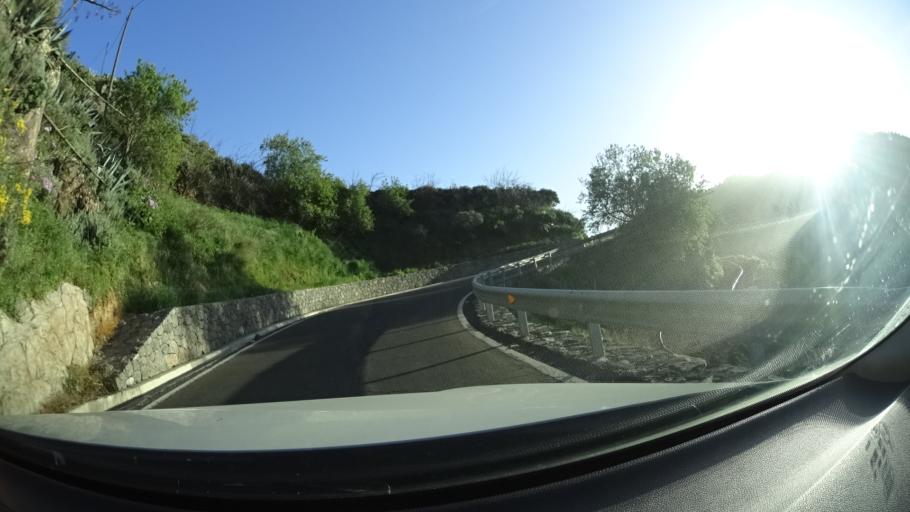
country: ES
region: Canary Islands
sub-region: Provincia de Las Palmas
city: Artenara
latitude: 28.0339
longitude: -15.6696
